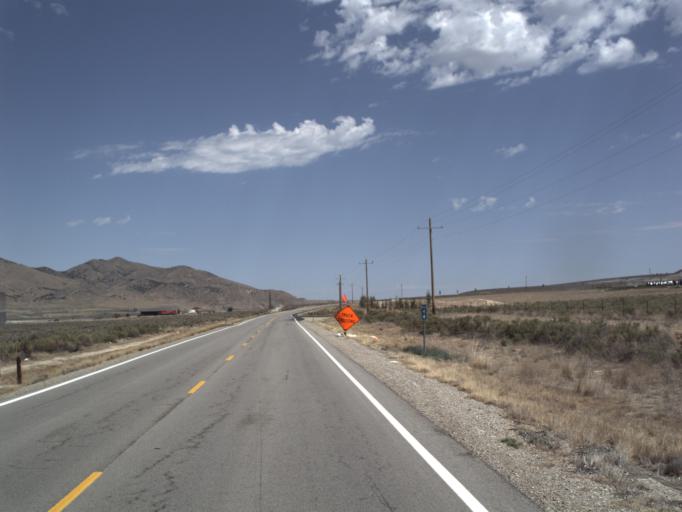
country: US
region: Utah
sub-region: Tooele County
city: Tooele
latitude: 40.3990
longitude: -112.3860
